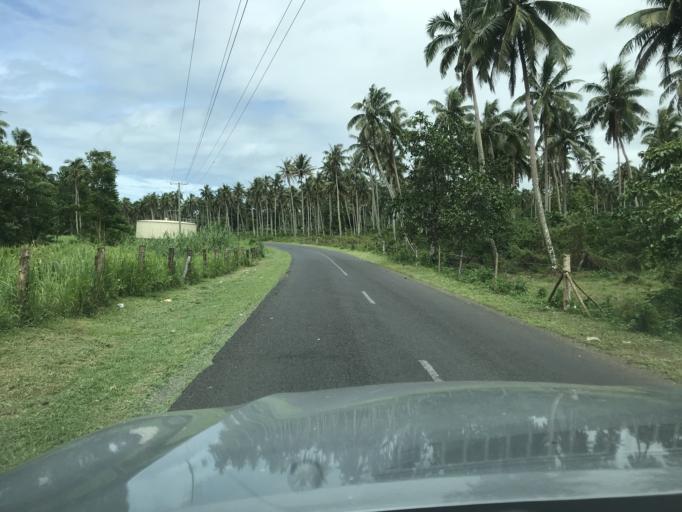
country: WS
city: Fasito`outa
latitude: -13.8728
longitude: -171.9168
